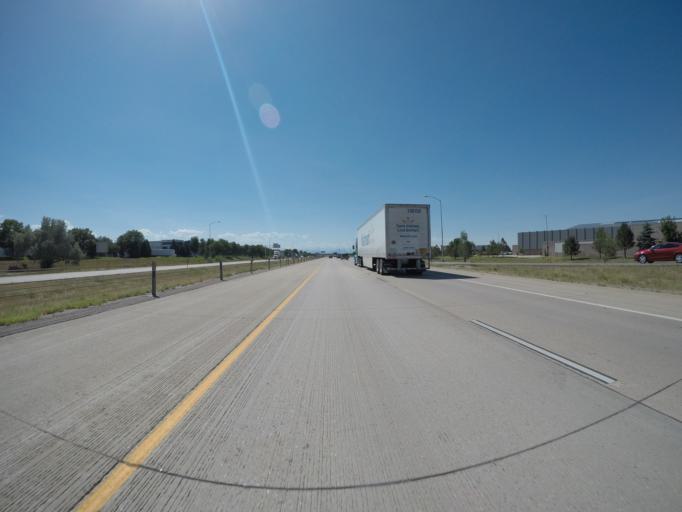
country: US
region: Colorado
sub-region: Adams County
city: Aurora
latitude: 39.7602
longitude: -104.7747
